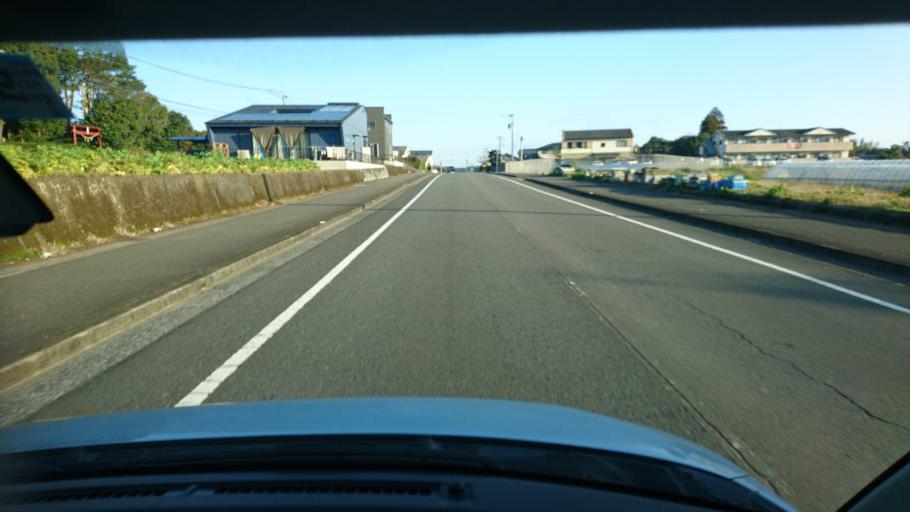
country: JP
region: Miyazaki
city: Miyazaki-shi
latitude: 31.8332
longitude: 131.4199
